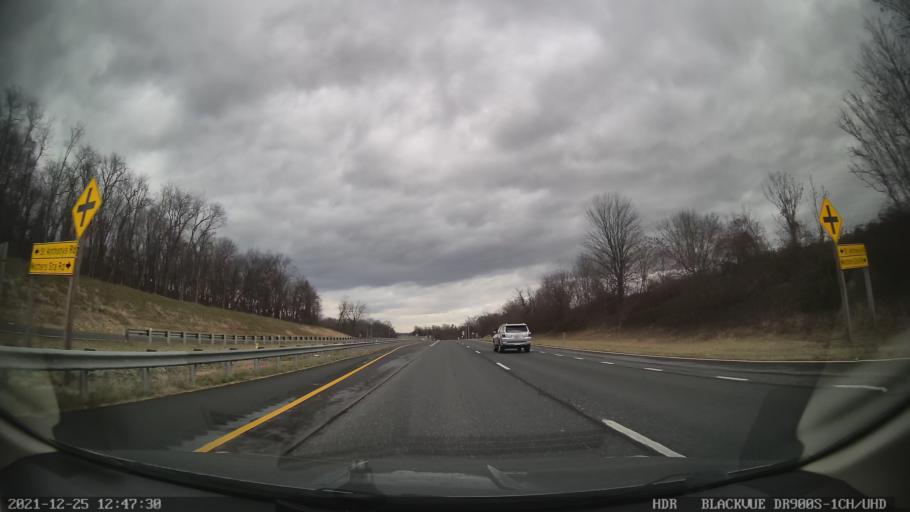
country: US
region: Maryland
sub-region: Frederick County
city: Emmitsburg
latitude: 39.6734
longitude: -77.3571
